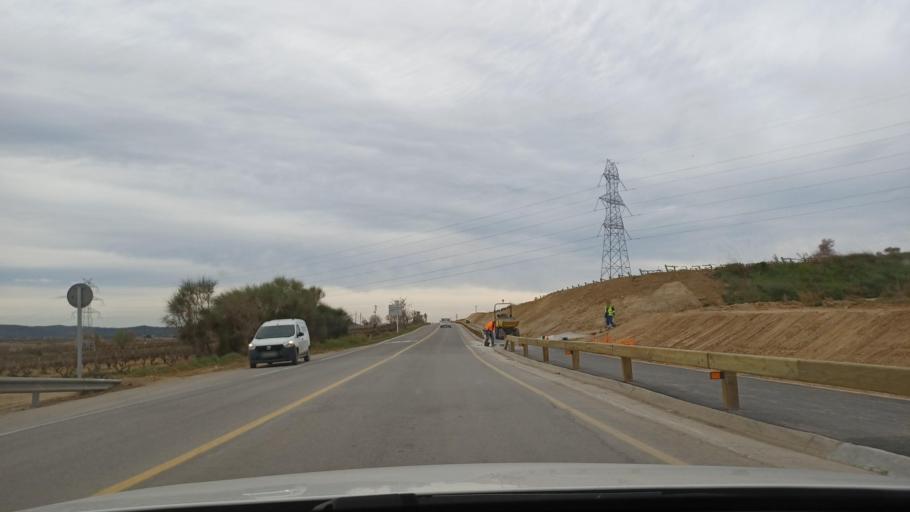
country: ES
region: Catalonia
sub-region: Provincia de Barcelona
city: Vilafranca del Penedes
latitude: 41.3674
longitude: 1.6917
